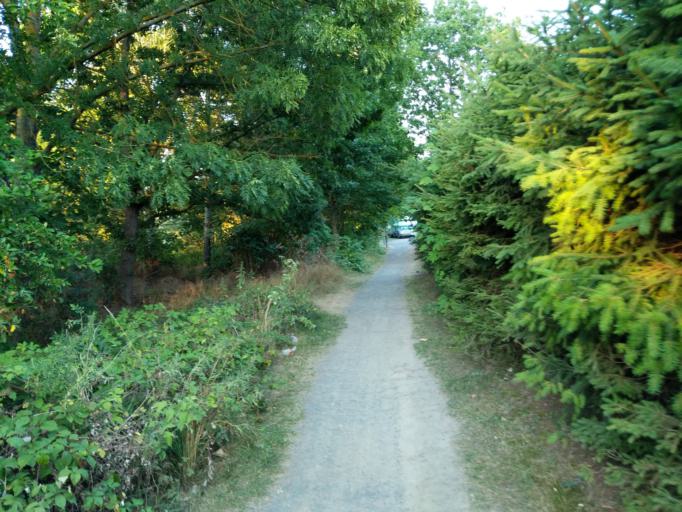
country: DE
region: Hesse
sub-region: Regierungsbezirk Kassel
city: Waldeck
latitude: 51.1839
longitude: 9.0251
